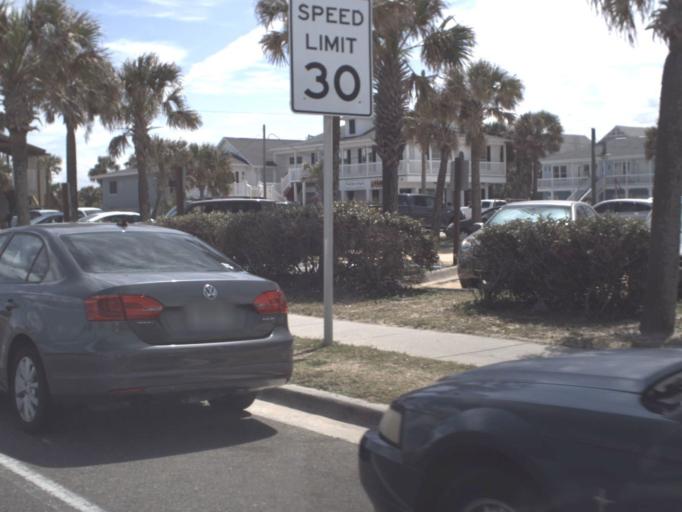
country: US
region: Florida
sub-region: Flagler County
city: Flagler Beach
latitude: 29.4781
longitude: -81.1260
